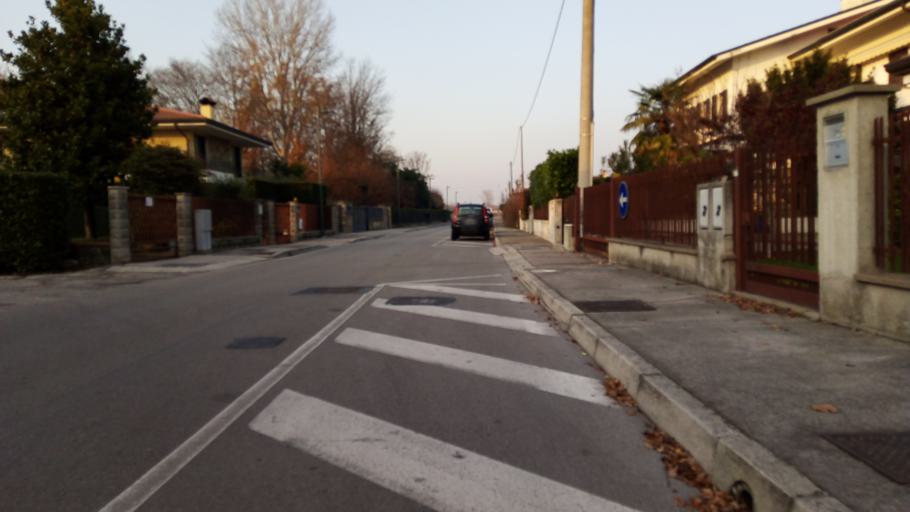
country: IT
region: Veneto
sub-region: Provincia di Padova
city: Abano Terme
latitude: 45.3572
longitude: 11.7713
